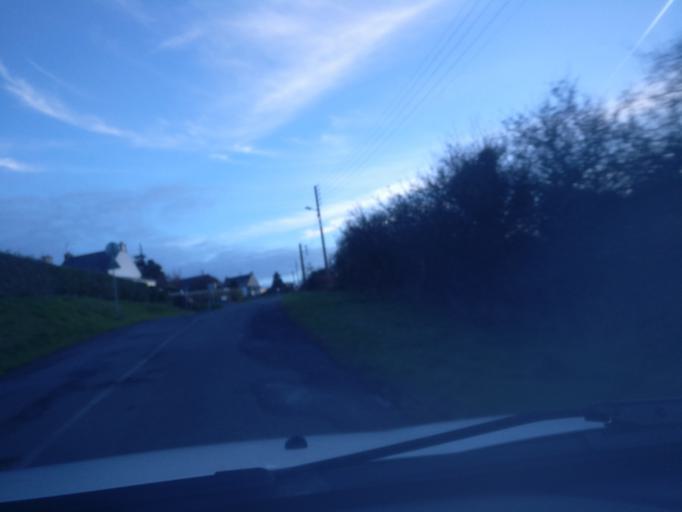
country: FR
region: Brittany
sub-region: Departement des Cotes-d'Armor
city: Tregastel
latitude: 48.8168
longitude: -3.4760
